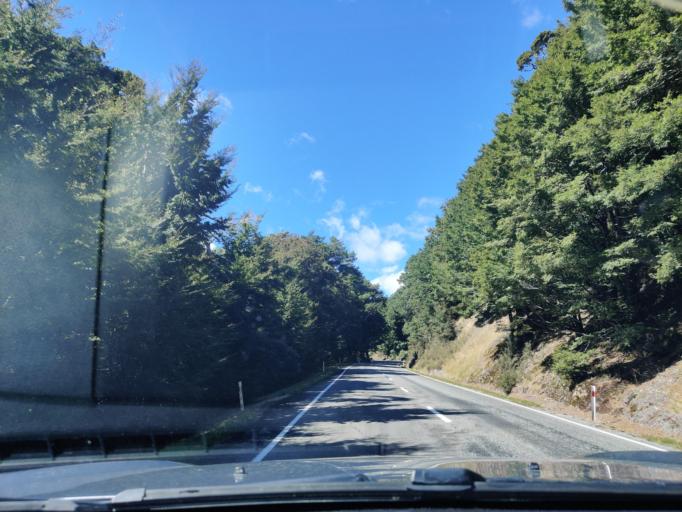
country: NZ
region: Canterbury
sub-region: Hurunui District
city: Amberley
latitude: -42.3746
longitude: 172.3682
